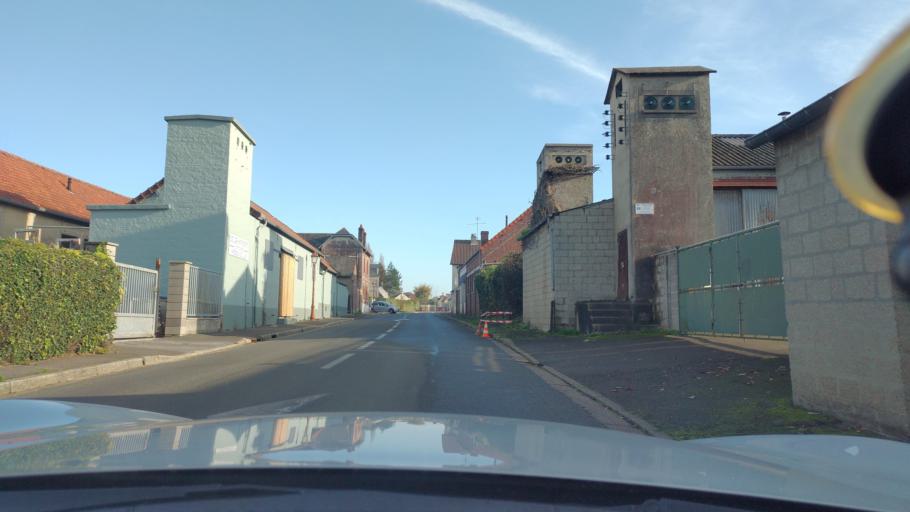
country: FR
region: Picardie
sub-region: Departement de la Somme
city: Fressenneville
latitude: 50.0684
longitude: 1.5695
